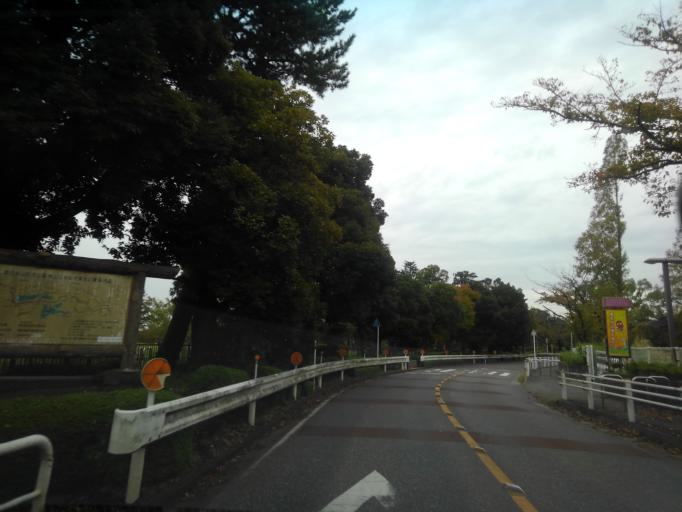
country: JP
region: Tokyo
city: Higashimurayama-shi
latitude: 35.7670
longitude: 139.4412
